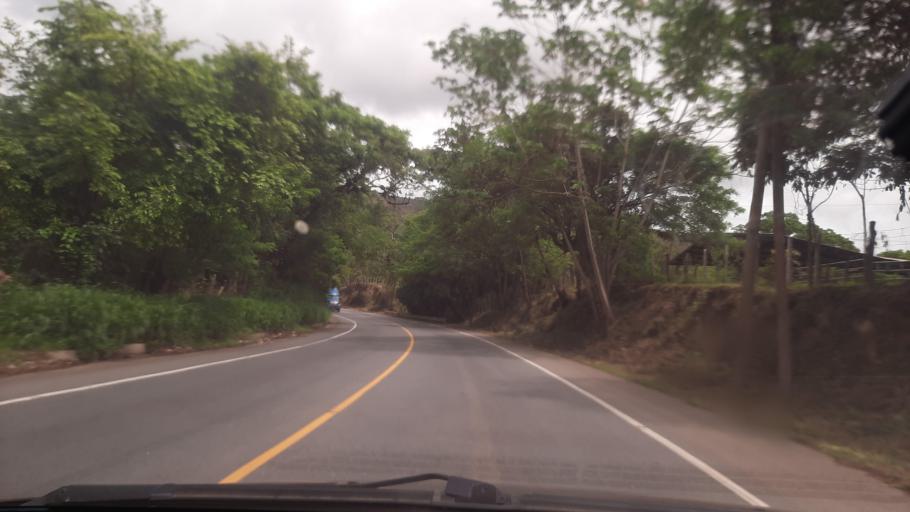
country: GT
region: Izabal
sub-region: Municipio de Los Amates
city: Los Amates
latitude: 15.2333
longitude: -89.1988
